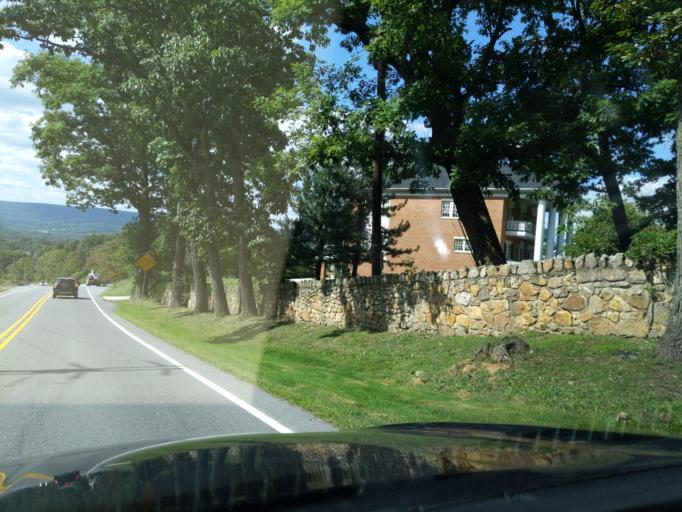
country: US
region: Pennsylvania
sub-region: Blair County
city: Greenwood
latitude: 40.5149
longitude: -78.3633
